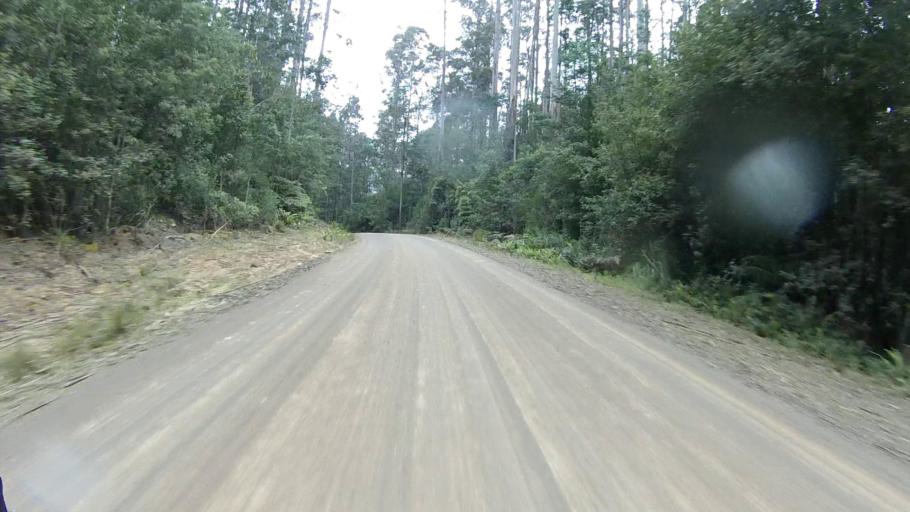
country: AU
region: Tasmania
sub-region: Sorell
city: Sorell
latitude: -42.7094
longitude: 147.8401
